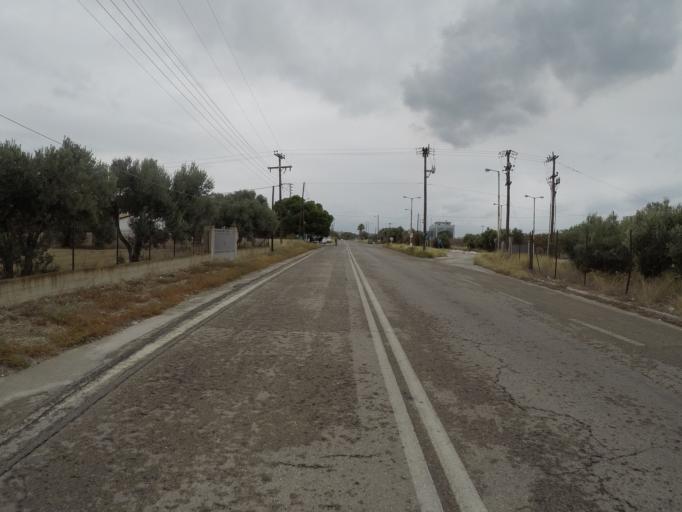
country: GR
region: Peloponnese
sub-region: Nomos Korinthias
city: Isthmia
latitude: 37.9210
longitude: 23.0302
